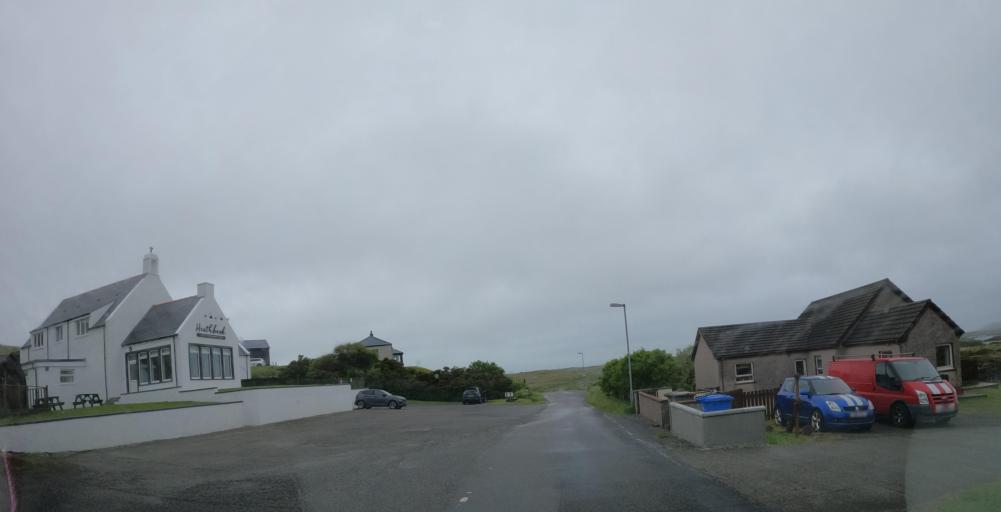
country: GB
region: Scotland
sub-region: Eilean Siar
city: Barra
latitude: 56.9976
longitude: -7.4198
